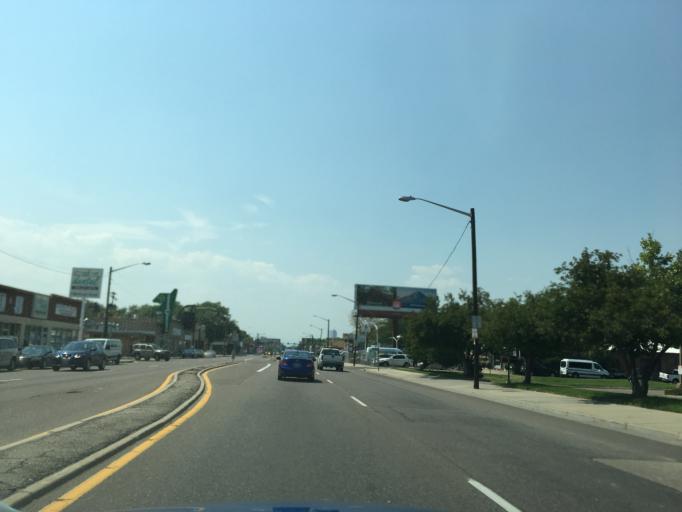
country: US
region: Colorado
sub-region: Arapahoe County
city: Glendale
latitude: 39.7402
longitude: -104.9259
